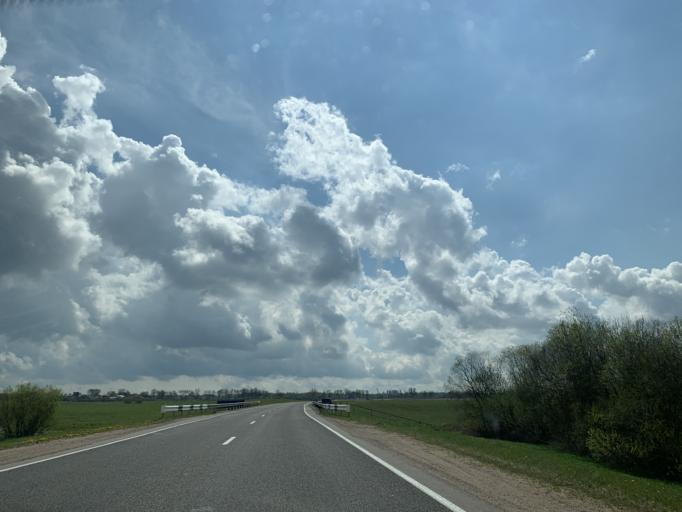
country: BY
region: Minsk
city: Nyasvizh
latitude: 53.2352
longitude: 26.7183
